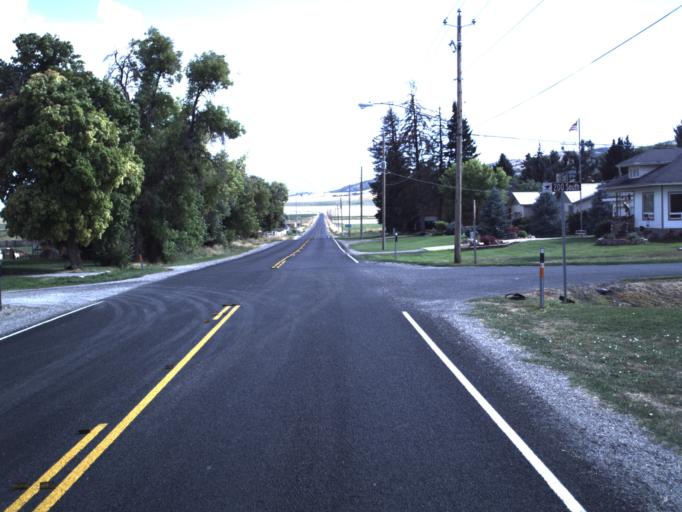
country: US
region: Utah
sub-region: Cache County
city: Benson
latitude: 41.9161
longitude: -112.0452
